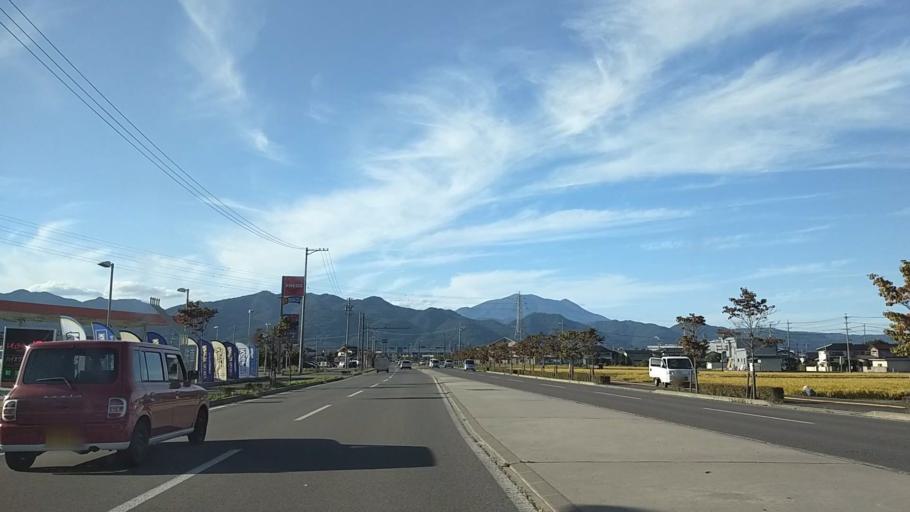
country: JP
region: Nagano
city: Nagano-shi
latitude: 36.5986
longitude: 138.1814
